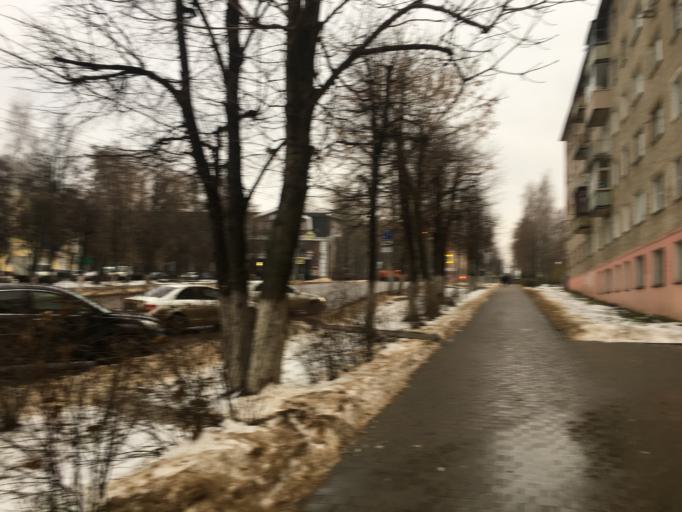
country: RU
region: Tula
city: Tula
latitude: 54.1931
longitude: 37.5840
